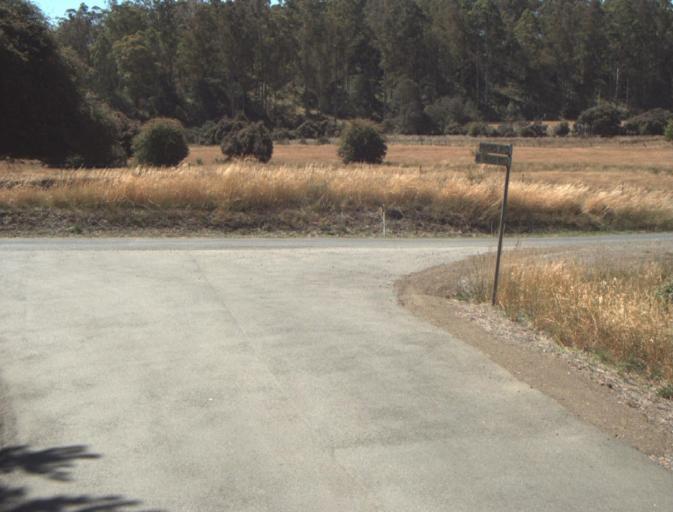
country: AU
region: Tasmania
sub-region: Dorset
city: Scottsdale
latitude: -41.3145
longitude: 147.3812
